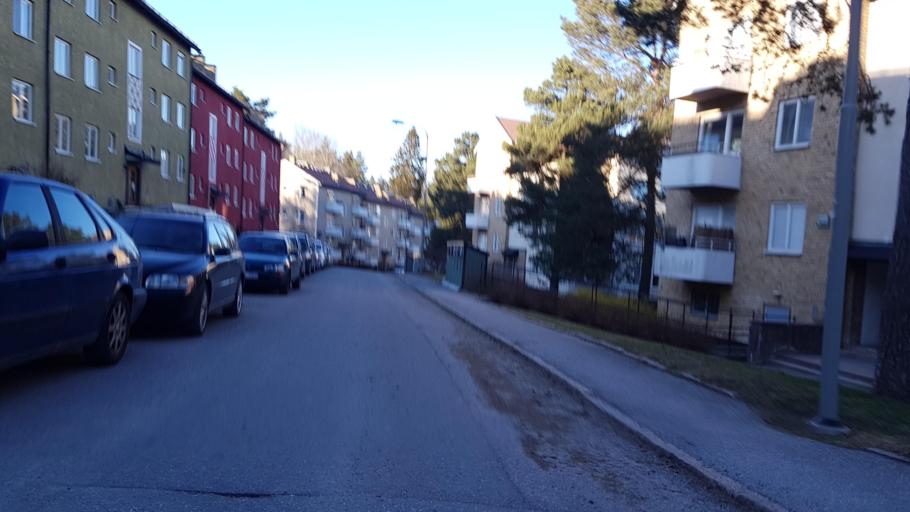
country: SE
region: Stockholm
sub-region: Stockholms Kommun
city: Arsta
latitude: 59.2647
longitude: 18.0754
